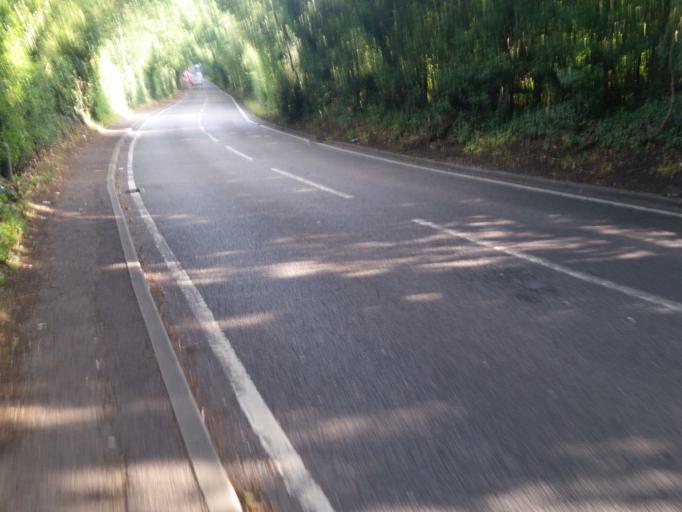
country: GB
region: England
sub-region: Greater London
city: High Barnet
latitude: 51.6329
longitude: -0.2359
